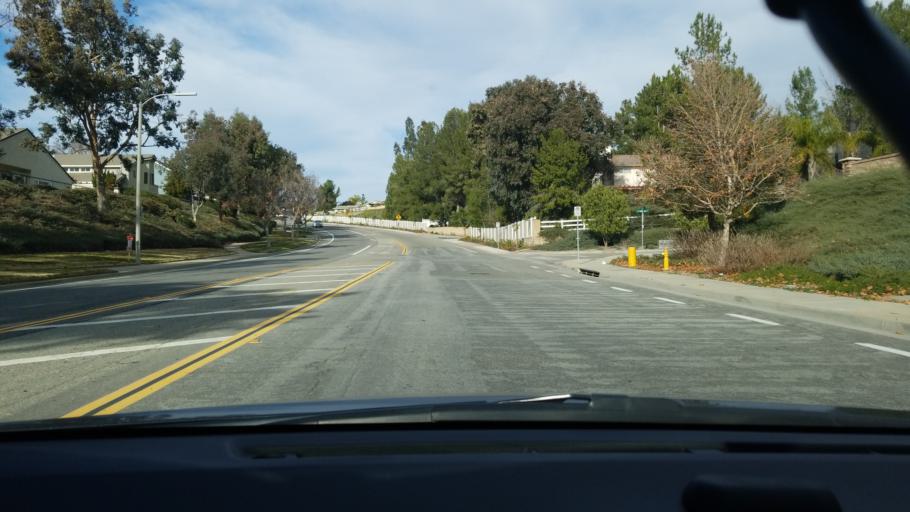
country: US
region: California
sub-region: Riverside County
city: Temecula
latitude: 33.4930
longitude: -117.1387
